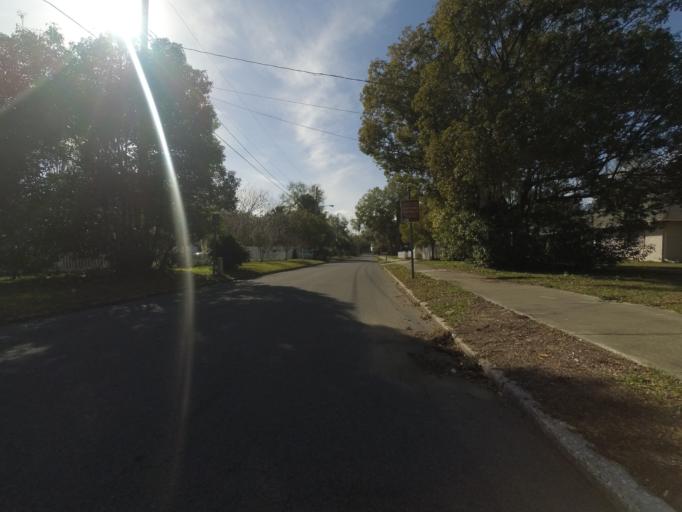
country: US
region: Florida
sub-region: Lake County
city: Mount Dora
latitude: 28.8042
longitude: -81.6368
